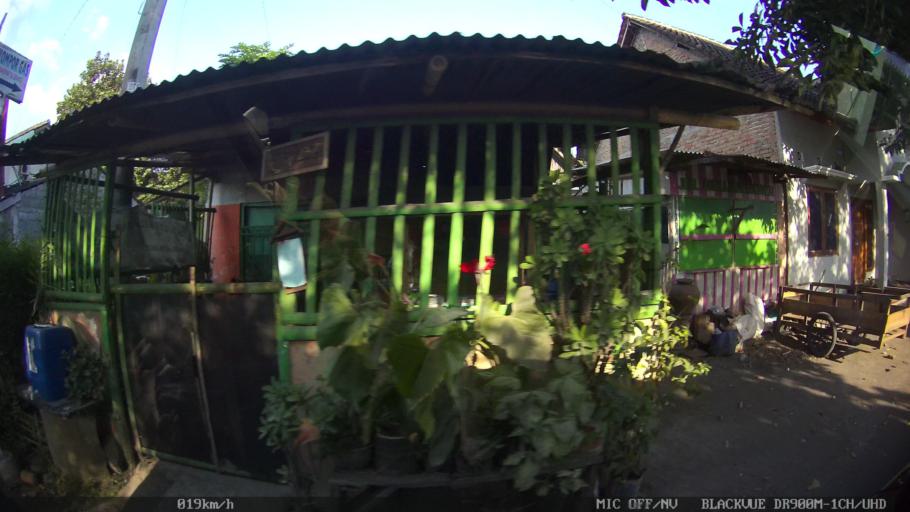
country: ID
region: Daerah Istimewa Yogyakarta
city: Gamping Lor
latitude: -7.7962
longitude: 110.3328
